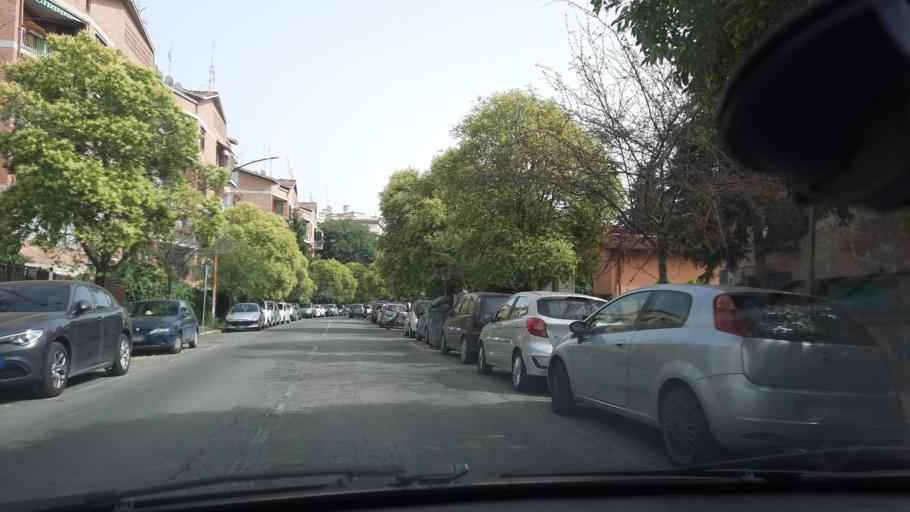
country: IT
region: Latium
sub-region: Citta metropolitana di Roma Capitale
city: Rome
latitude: 41.8636
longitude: 12.4926
